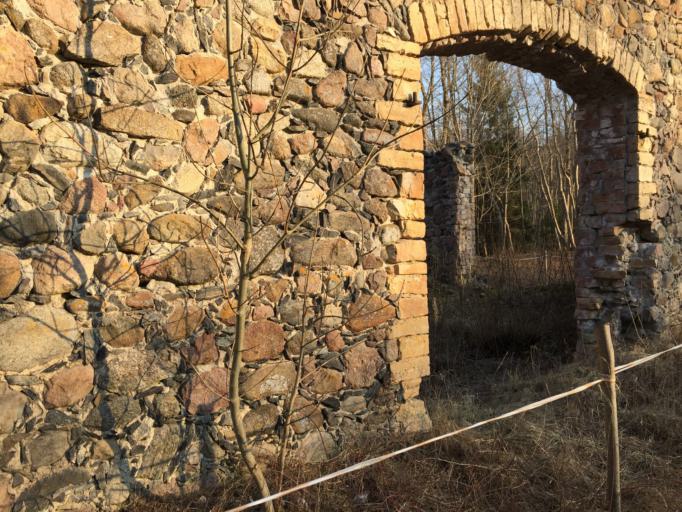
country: EE
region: Laeaene
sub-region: Lihula vald
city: Lihula
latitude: 58.5315
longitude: 23.6981
